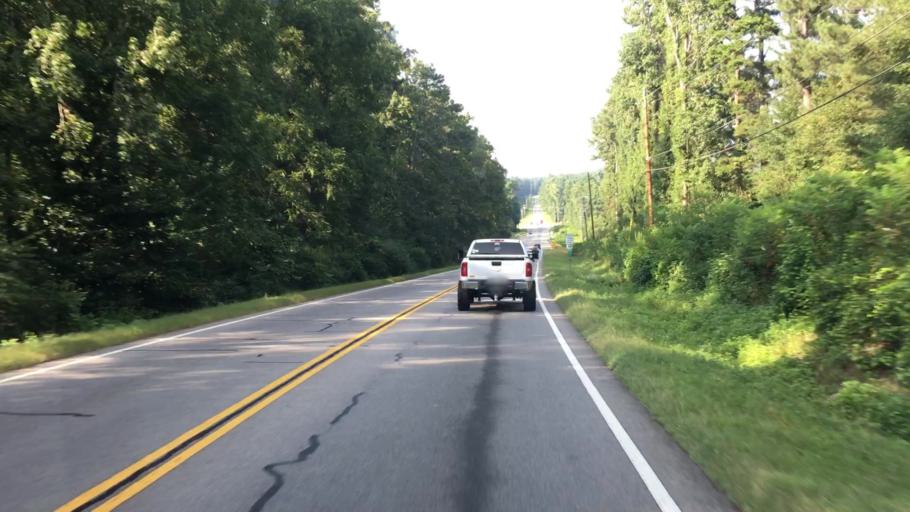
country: US
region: Georgia
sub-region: Barrow County
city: Russell
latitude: 33.9554
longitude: -83.7212
